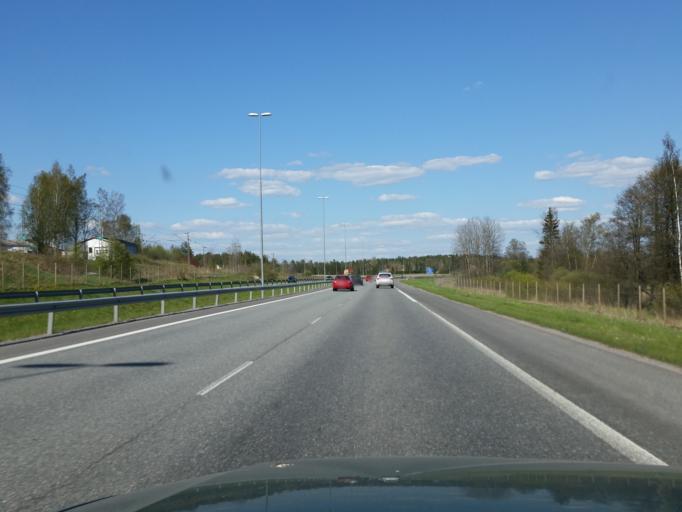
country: FI
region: Uusimaa
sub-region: Helsinki
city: Kirkkonummi
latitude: 60.1263
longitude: 24.4911
